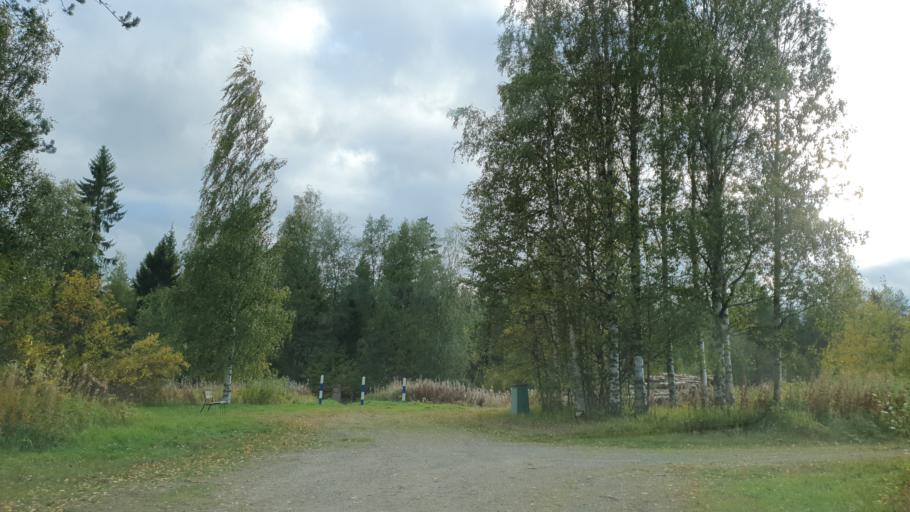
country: FI
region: Kainuu
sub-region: Kehys-Kainuu
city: Kuhmo
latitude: 63.9476
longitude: 29.8816
